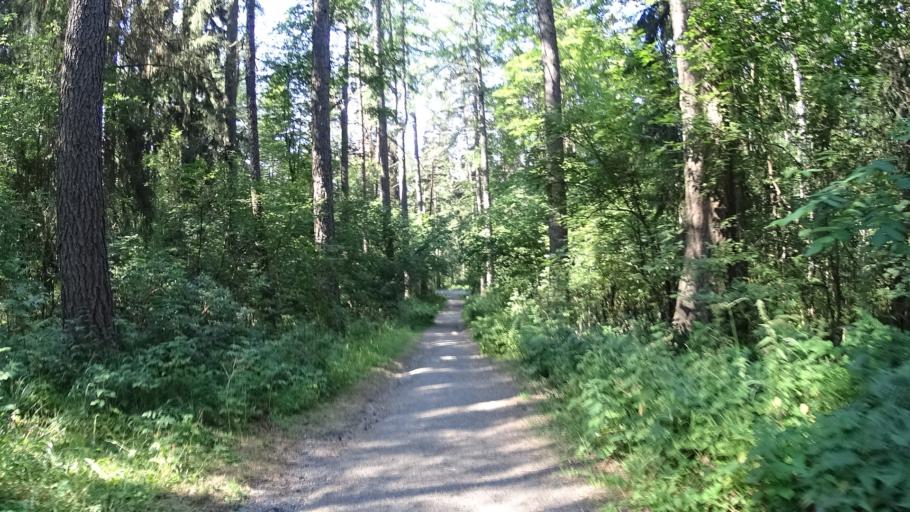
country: FI
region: Haeme
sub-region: Haemeenlinna
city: Haemeenlinna
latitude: 61.0229
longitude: 24.4512
